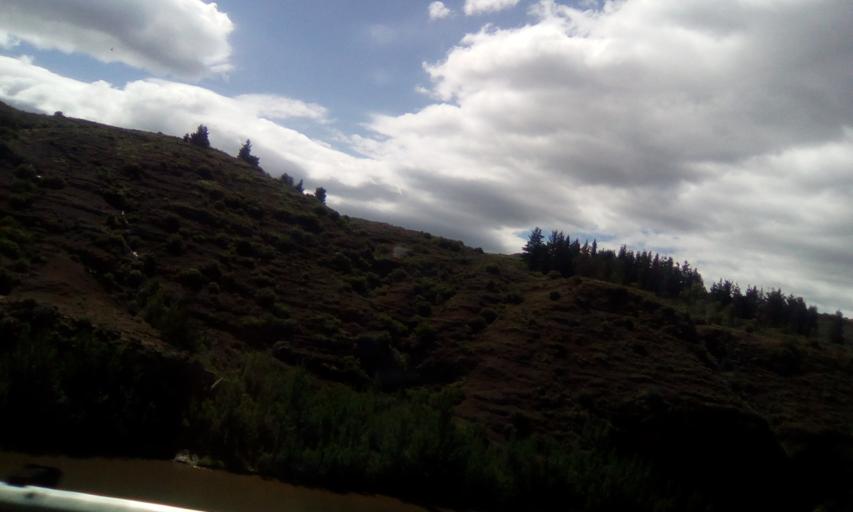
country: LS
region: Maseru
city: Nako
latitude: -29.6680
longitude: 27.8005
